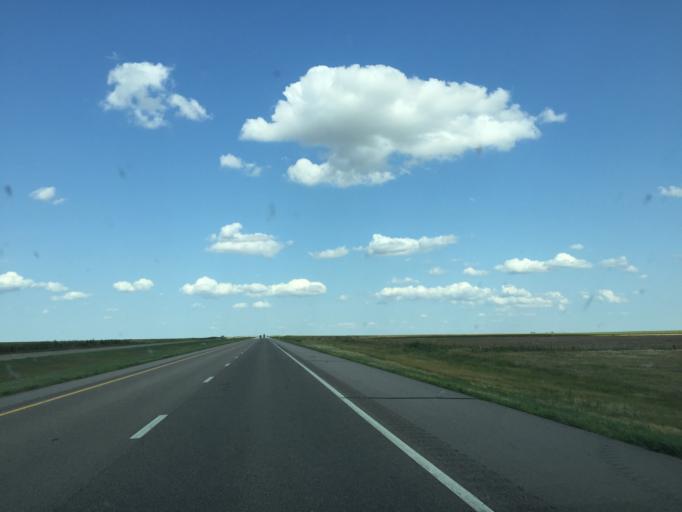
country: US
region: Kansas
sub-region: Trego County
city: WaKeeney
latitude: 39.0230
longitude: -100.0386
